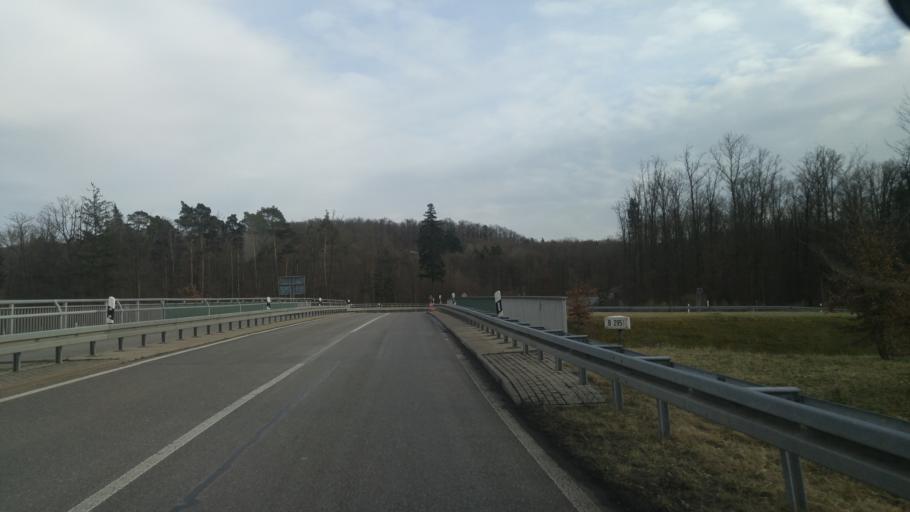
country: DE
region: Baden-Wuerttemberg
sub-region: Regierungsbezirk Stuttgart
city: Renningen
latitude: 48.7815
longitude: 8.9714
